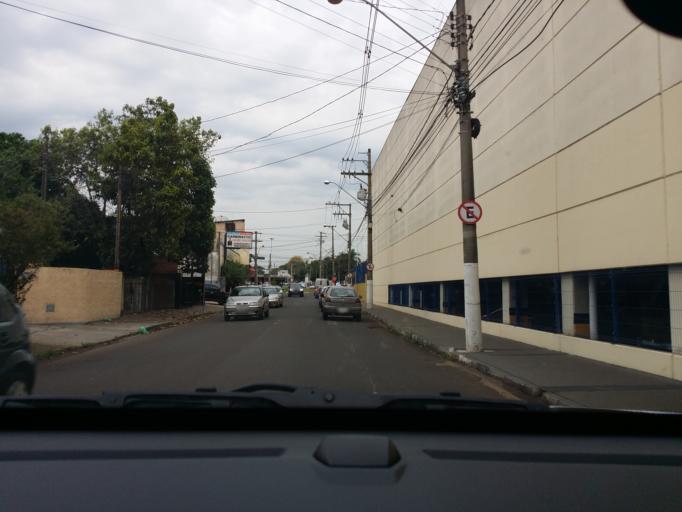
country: BR
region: Sao Paulo
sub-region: Sao Carlos
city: Sao Carlos
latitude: -22.0314
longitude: -47.8914
